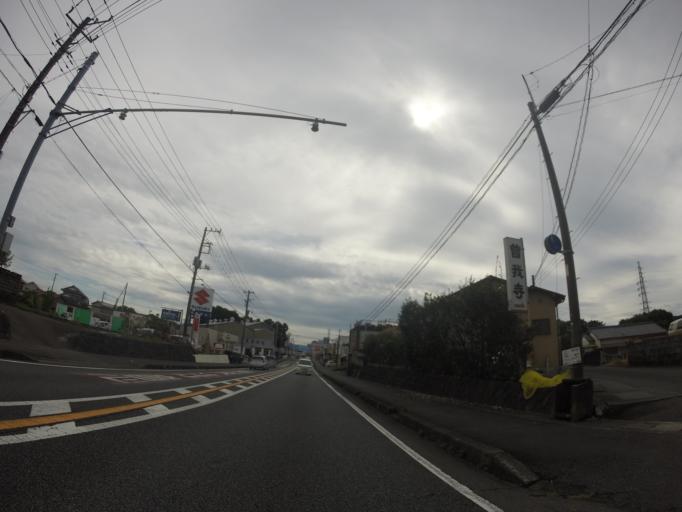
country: JP
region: Shizuoka
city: Fuji
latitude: 35.1896
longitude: 138.6518
